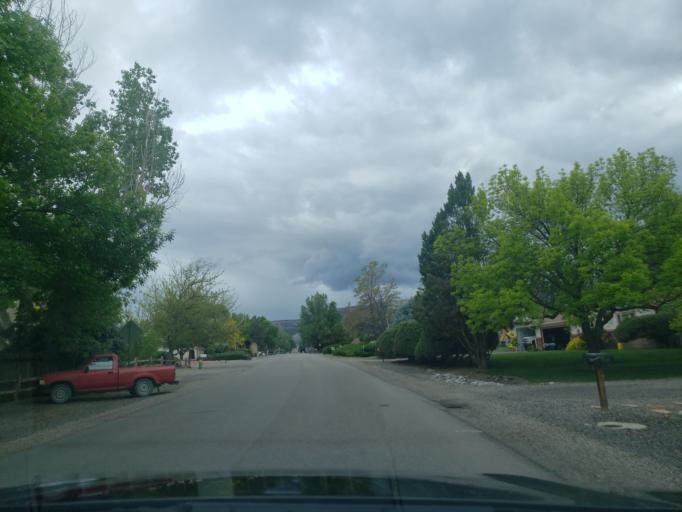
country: US
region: Colorado
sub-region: Mesa County
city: Redlands
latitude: 39.0979
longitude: -108.6622
